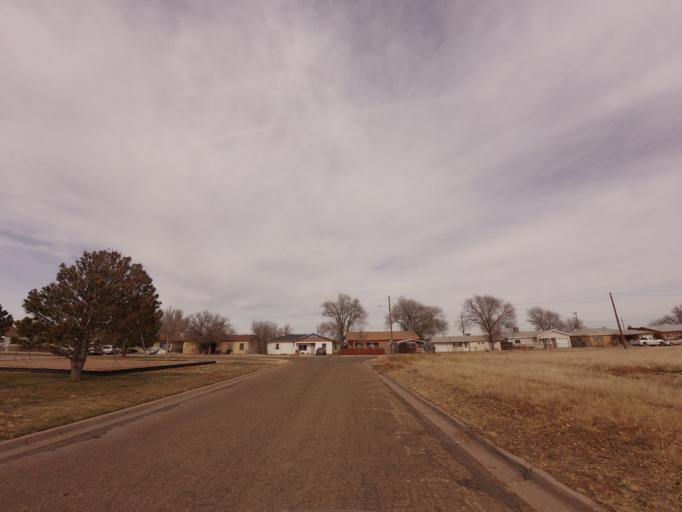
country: US
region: New Mexico
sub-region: Curry County
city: Clovis
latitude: 34.4032
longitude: -103.2437
